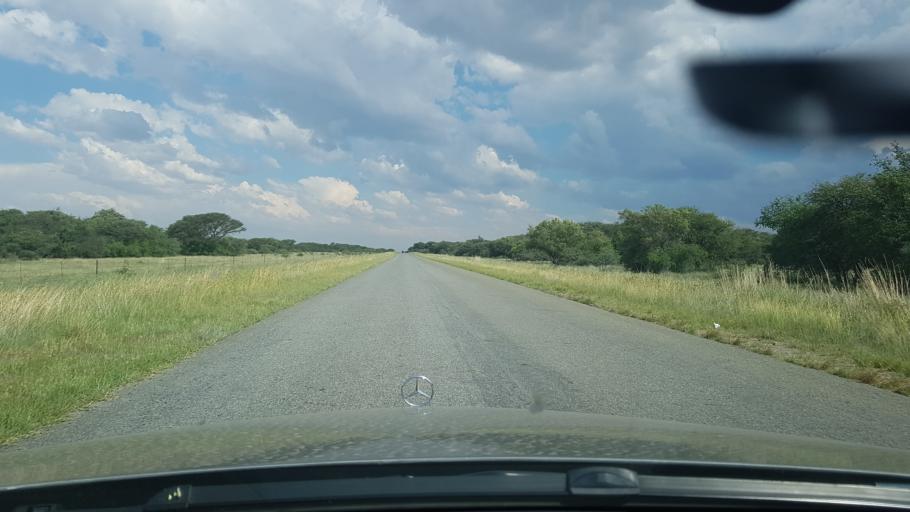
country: ZA
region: North-West
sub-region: Dr Ruth Segomotsi Mompati District Municipality
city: Bloemhof
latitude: -27.7996
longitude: 25.6194
